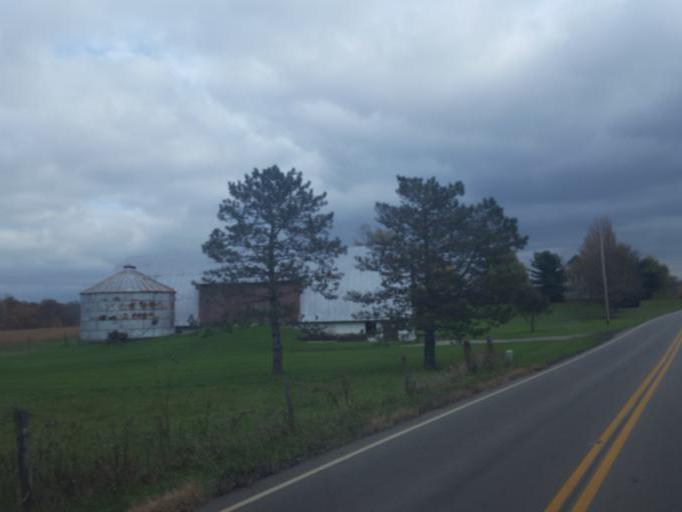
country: US
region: Ohio
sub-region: Crawford County
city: Crestline
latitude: 40.7015
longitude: -82.6997
